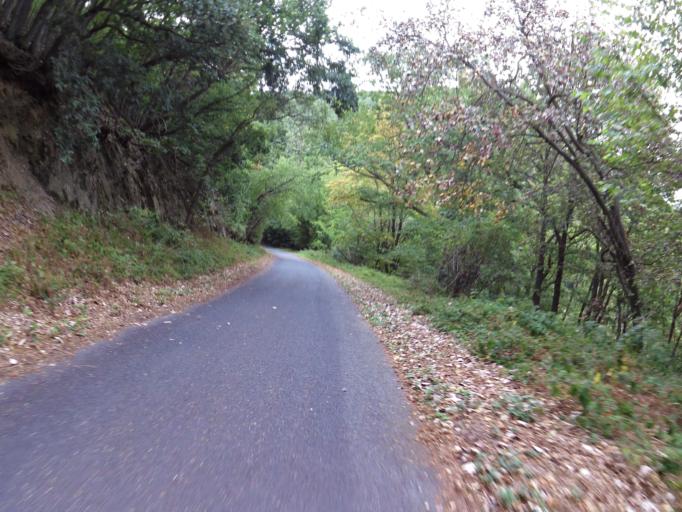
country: DE
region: North Rhine-Westphalia
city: Heimbach
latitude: 50.6202
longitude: 6.3964
